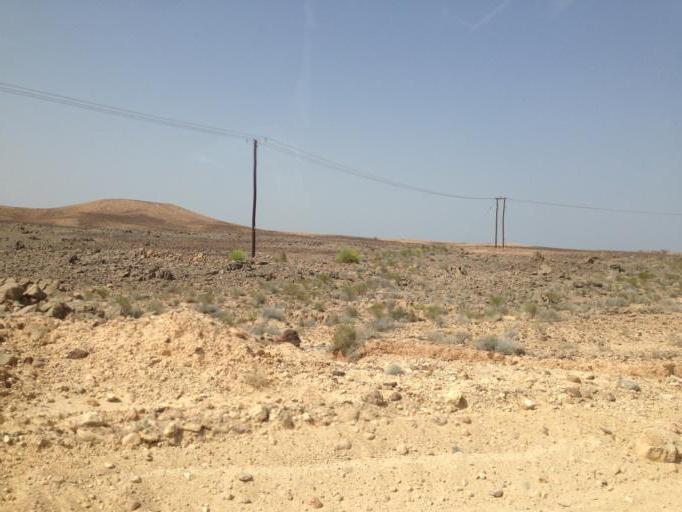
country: OM
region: Ash Sharqiyah
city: Ibra'
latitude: 23.0836
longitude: 58.9148
